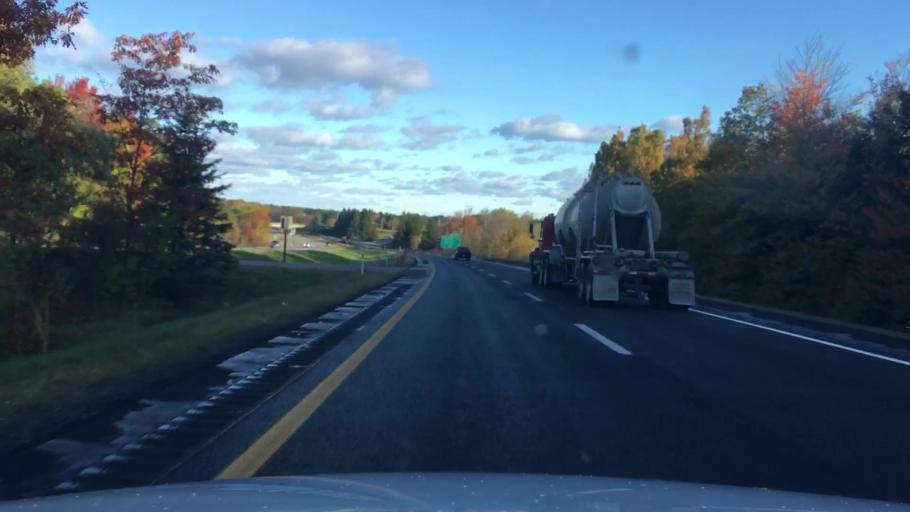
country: US
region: Maine
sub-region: Penobscot County
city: Orono
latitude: 44.8972
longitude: -68.6906
